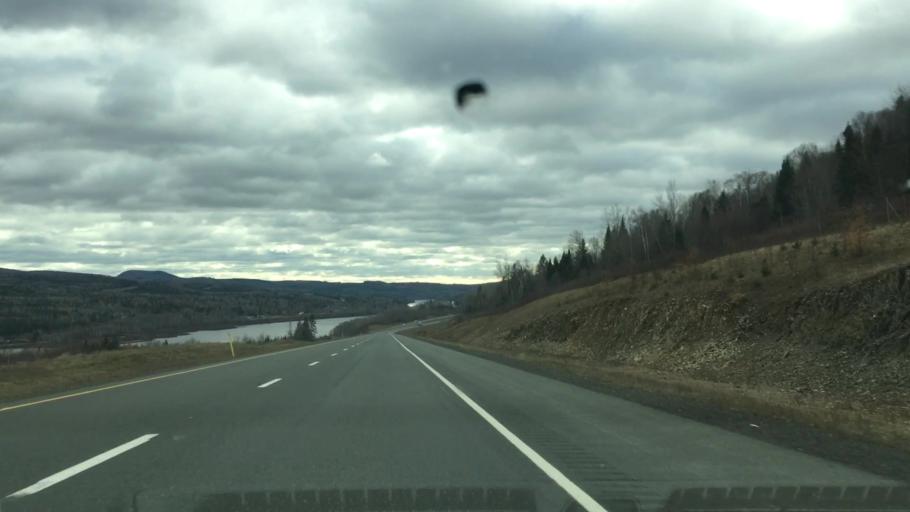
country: US
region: Maine
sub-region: Aroostook County
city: Fort Fairfield
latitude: 46.6860
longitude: -67.7349
